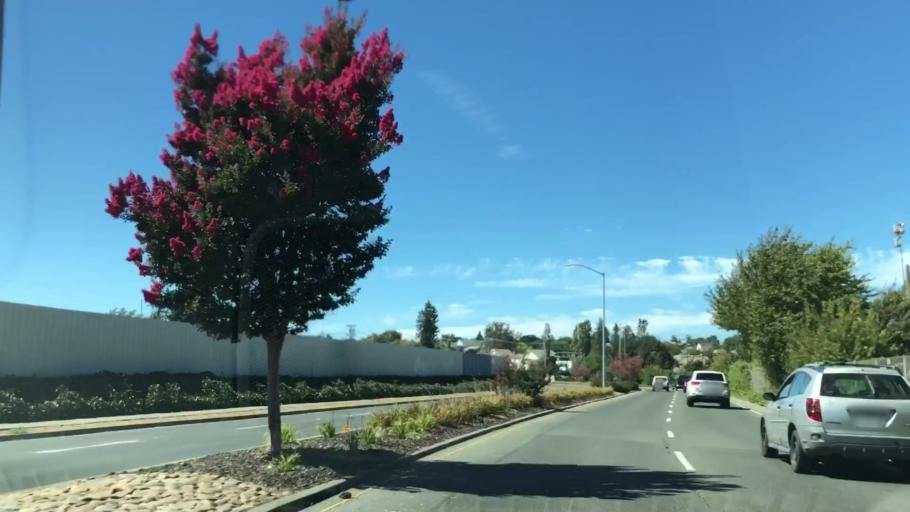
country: US
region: California
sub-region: Solano County
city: Vallejo
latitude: 38.0956
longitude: -122.2443
